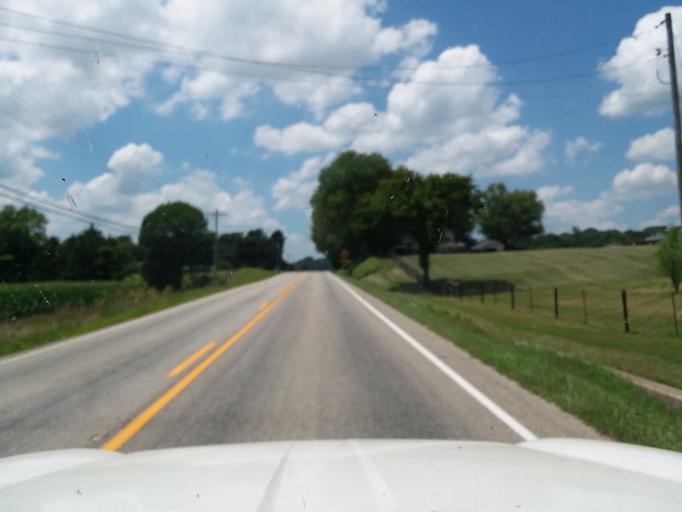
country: US
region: Indiana
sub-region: Johnson County
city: Trafalgar
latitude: 39.3721
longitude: -86.2900
